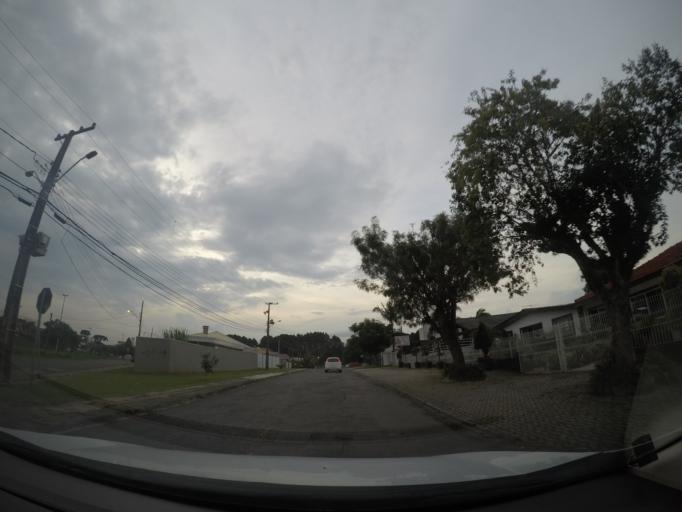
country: BR
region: Parana
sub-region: Sao Jose Dos Pinhais
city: Sao Jose dos Pinhais
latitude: -25.5134
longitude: -49.2357
